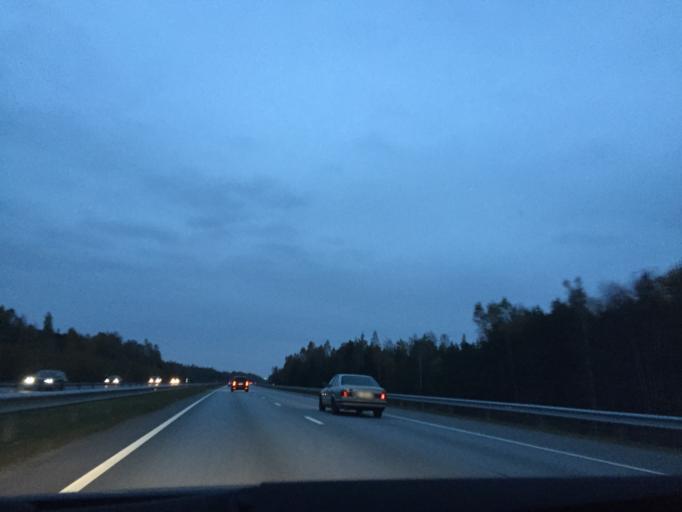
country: LV
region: Marupe
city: Marupe
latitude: 56.8656
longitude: 24.0661
